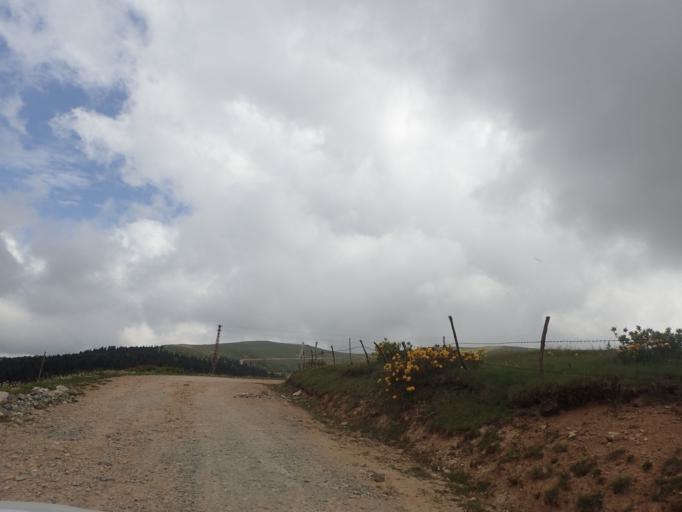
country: TR
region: Ordu
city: Topcam
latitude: 40.6379
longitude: 37.9374
